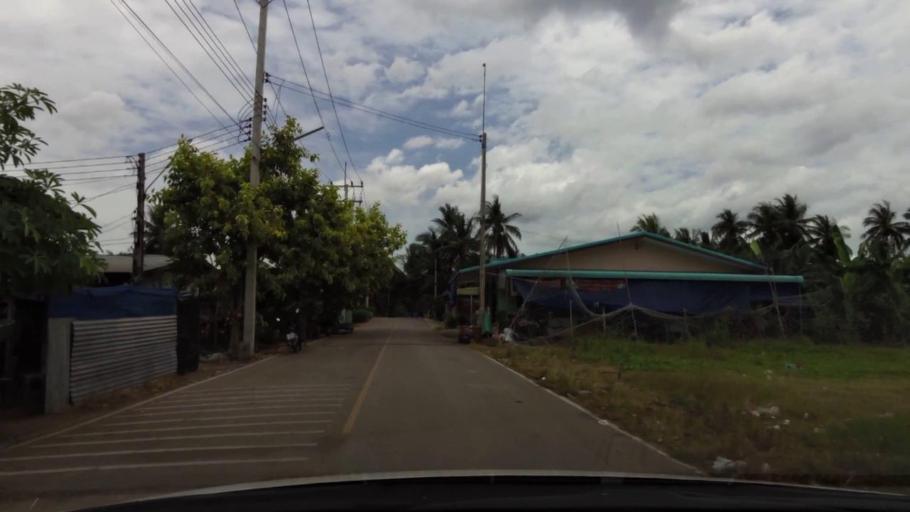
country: TH
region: Samut Sakhon
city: Ban Phaeo
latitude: 13.5693
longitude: 100.0353
